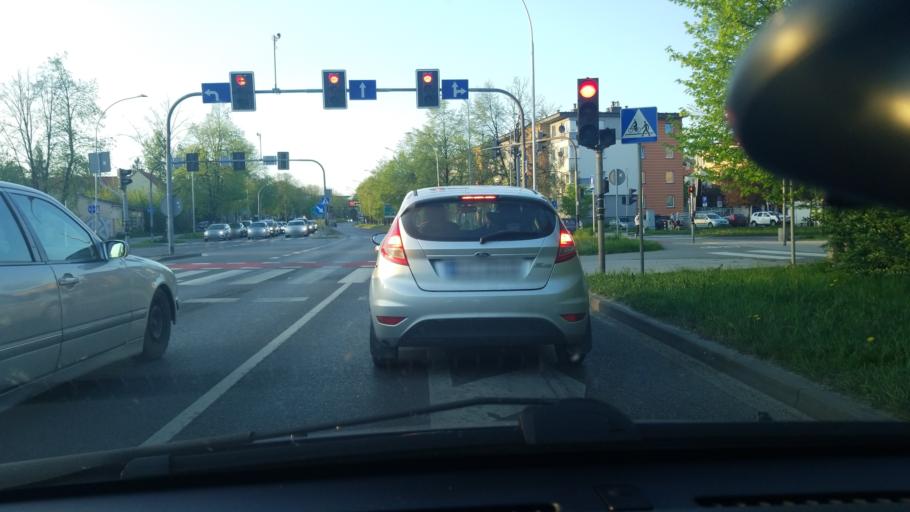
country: PL
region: Silesian Voivodeship
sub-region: Czestochowa
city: Czestochowa
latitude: 50.8050
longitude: 19.1031
